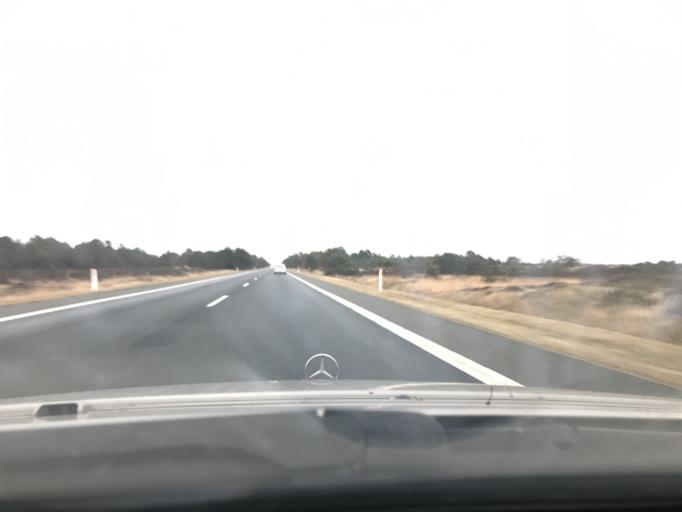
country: DE
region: Schleswig-Holstein
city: List
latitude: 55.1488
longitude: 8.5227
